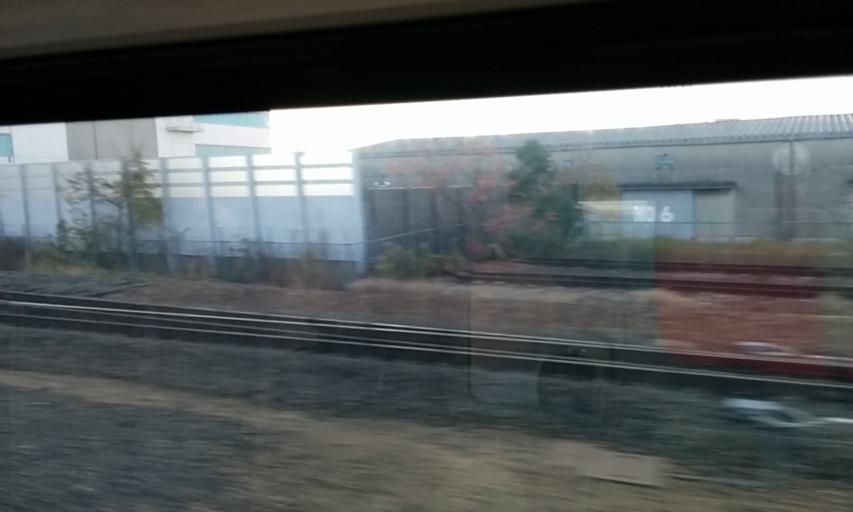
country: JP
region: Aichi
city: Kasugai
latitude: 35.2094
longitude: 136.9522
